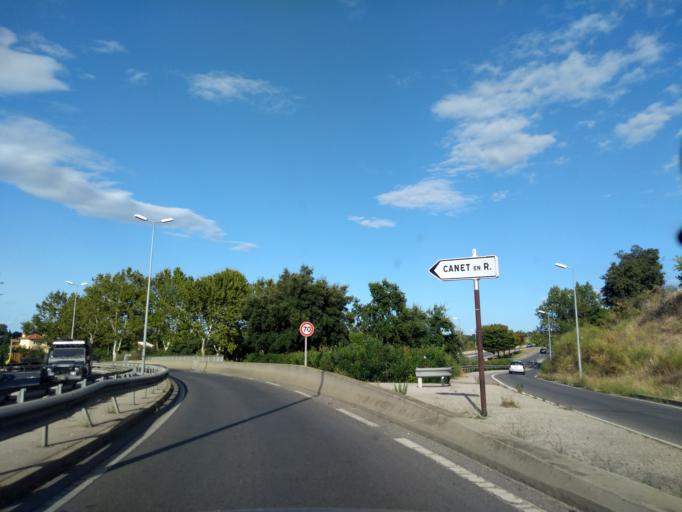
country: FR
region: Languedoc-Roussillon
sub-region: Departement des Pyrenees-Orientales
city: Perpignan
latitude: 42.6992
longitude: 2.9082
